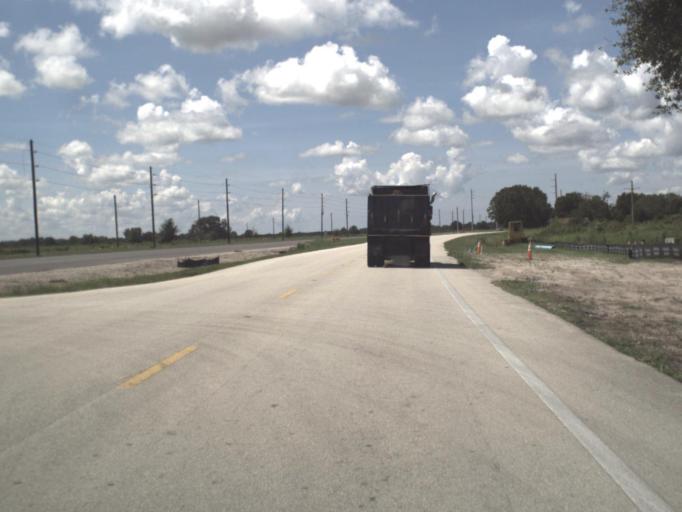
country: US
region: Florida
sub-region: DeSoto County
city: Nocatee
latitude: 27.1332
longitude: -81.9023
